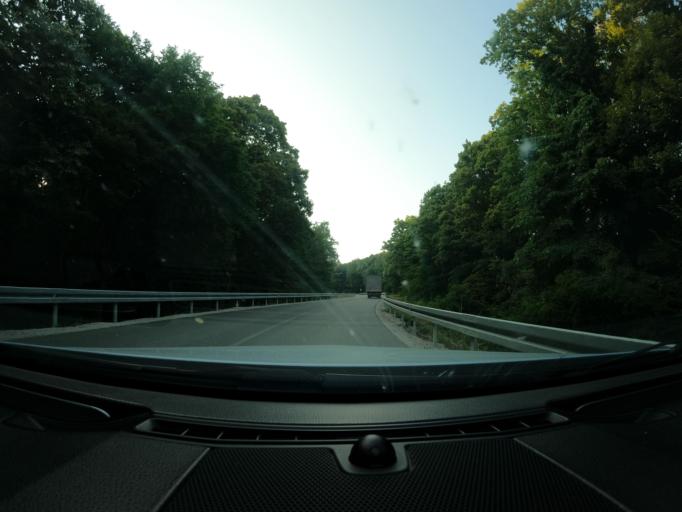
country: RS
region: Autonomna Pokrajina Vojvodina
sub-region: Juznobacki Okrug
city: Beocin
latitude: 45.1482
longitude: 19.7164
